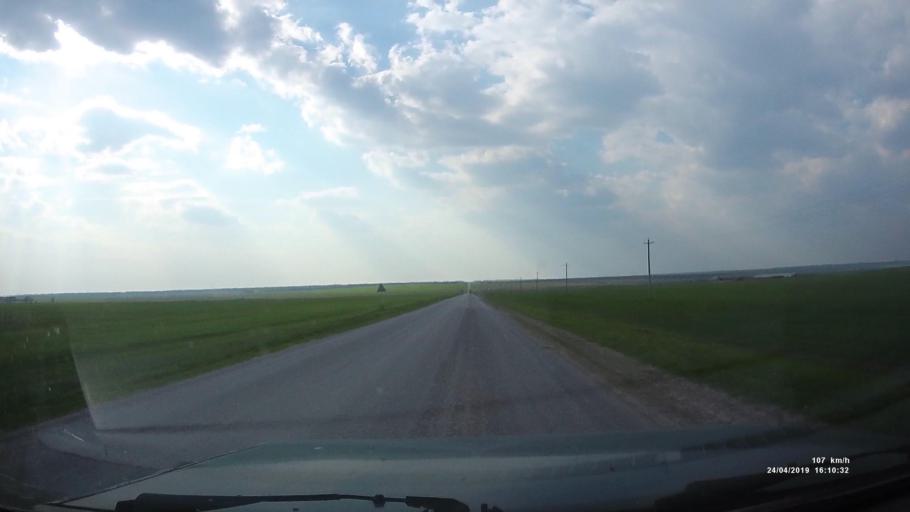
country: RU
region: Rostov
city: Sovetskoye
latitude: 46.7179
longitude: 42.2688
